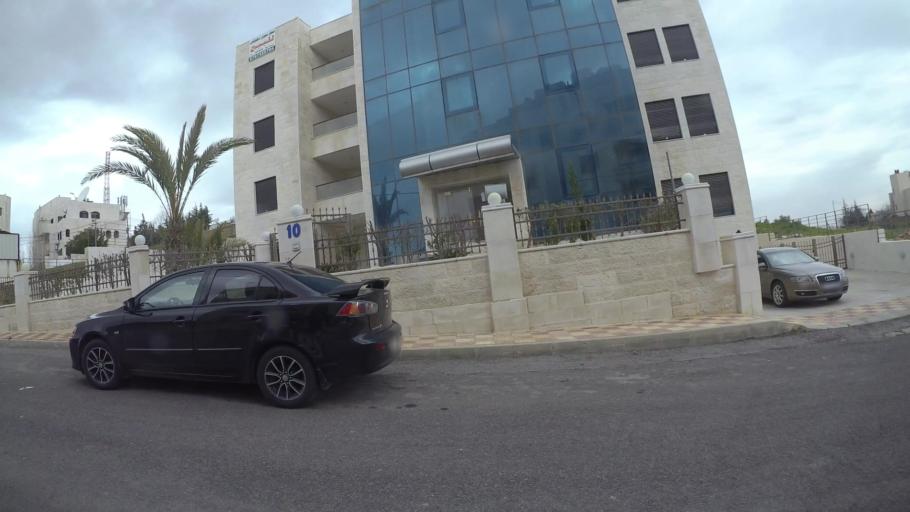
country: JO
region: Amman
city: Umm as Summaq
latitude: 31.9111
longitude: 35.8464
